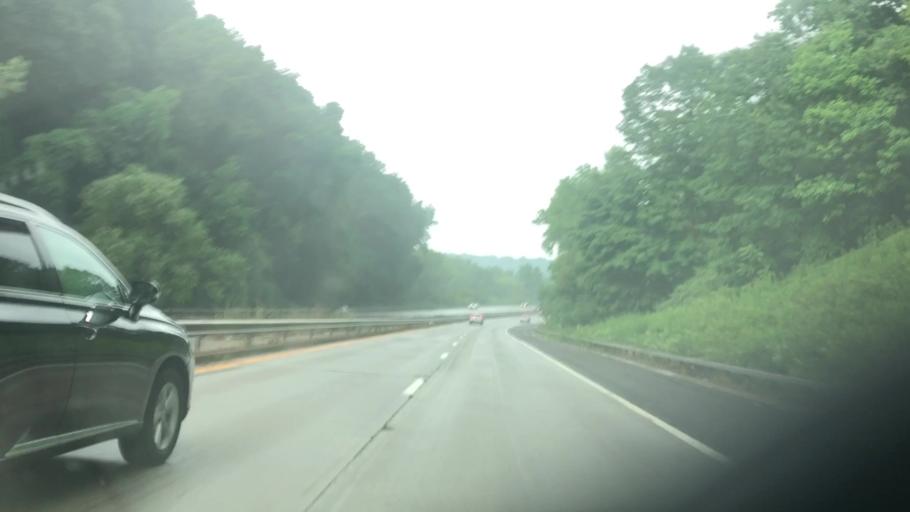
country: US
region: New York
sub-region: Monroe County
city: East Rochester
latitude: 43.1255
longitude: -77.5005
